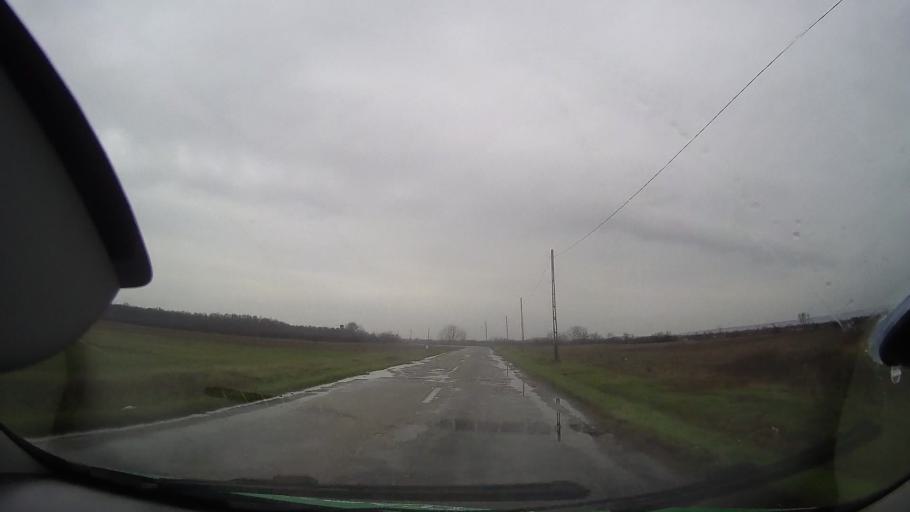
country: RO
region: Bihor
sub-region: Comuna Cociuba Mare
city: Cociuba Mare
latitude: 46.7415
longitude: 21.9810
